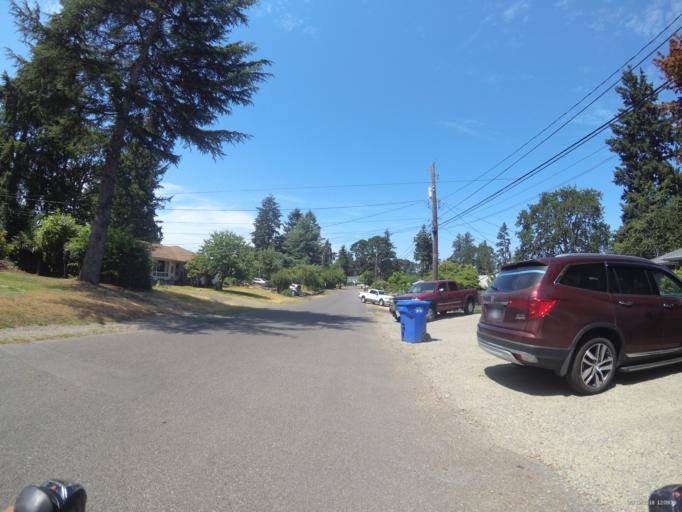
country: US
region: Washington
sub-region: Pierce County
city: Lakewood
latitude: 47.1760
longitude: -122.5310
